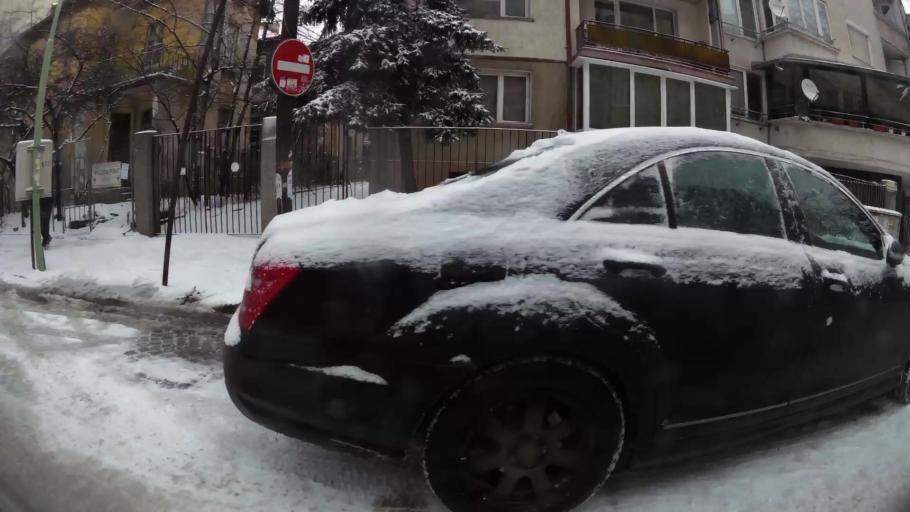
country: BG
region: Sofia-Capital
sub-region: Stolichna Obshtina
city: Sofia
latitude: 42.6875
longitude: 23.3043
